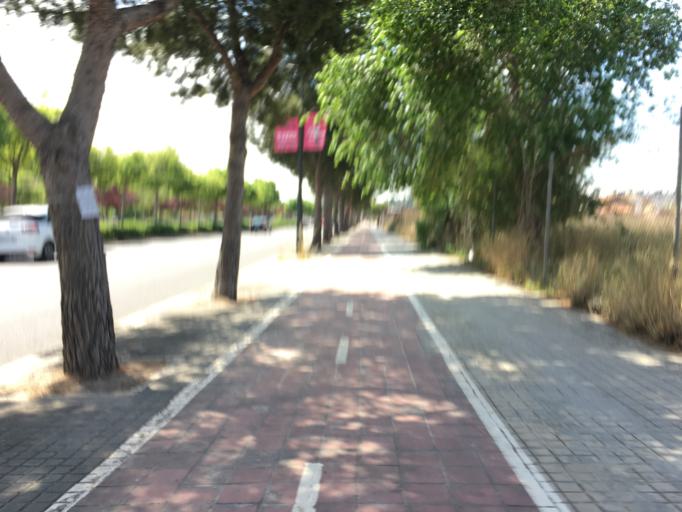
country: ES
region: Valencia
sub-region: Provincia de Valencia
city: Mislata
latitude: 39.4802
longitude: -0.4075
